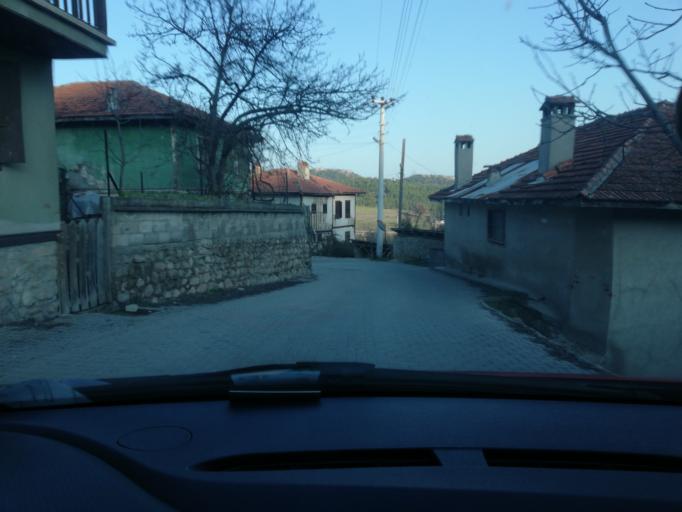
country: TR
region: Karabuk
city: Safranbolu
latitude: 41.2830
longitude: 32.6777
